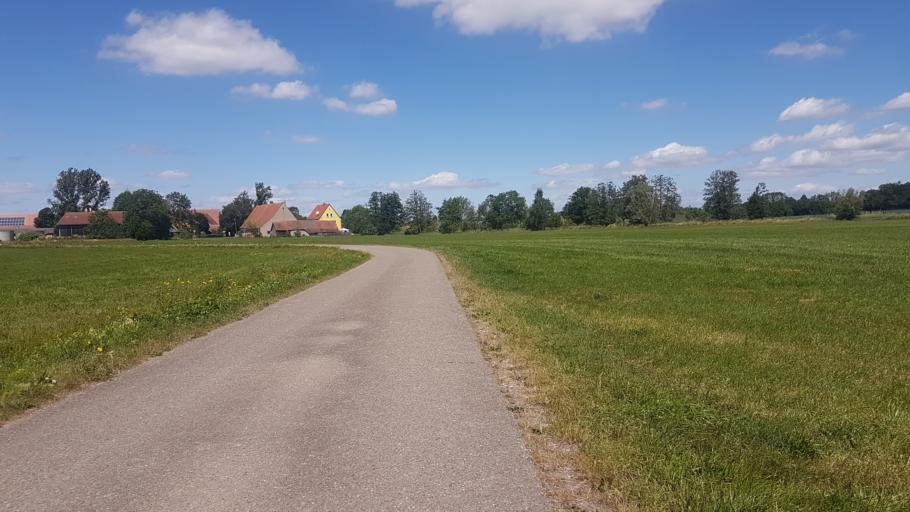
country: DE
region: Bavaria
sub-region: Regierungsbezirk Mittelfranken
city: Leutershausen
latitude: 49.2792
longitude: 10.4257
